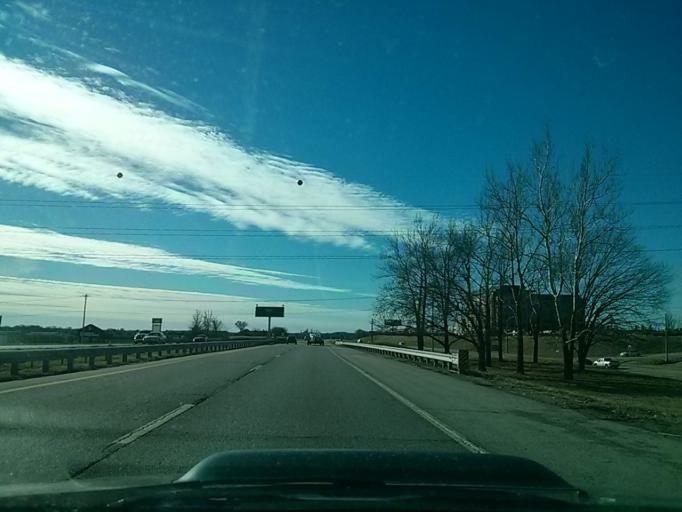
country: US
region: Oklahoma
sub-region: Tulsa County
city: Jenks
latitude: 36.0479
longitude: -96.0071
